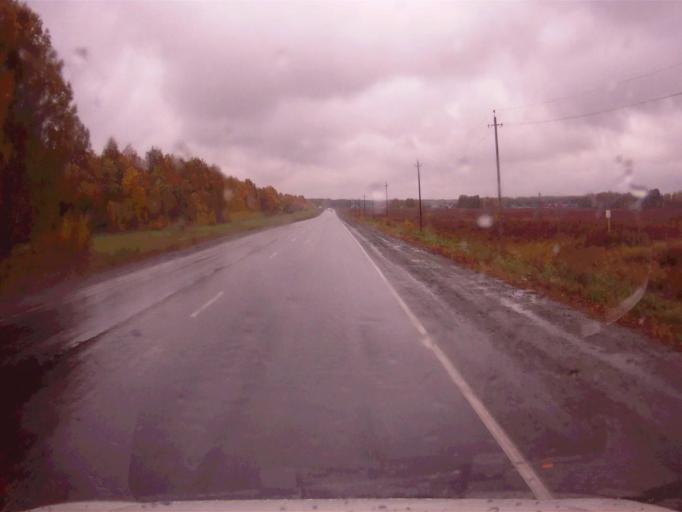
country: RU
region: Chelyabinsk
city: Argayash
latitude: 55.4029
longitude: 61.0673
